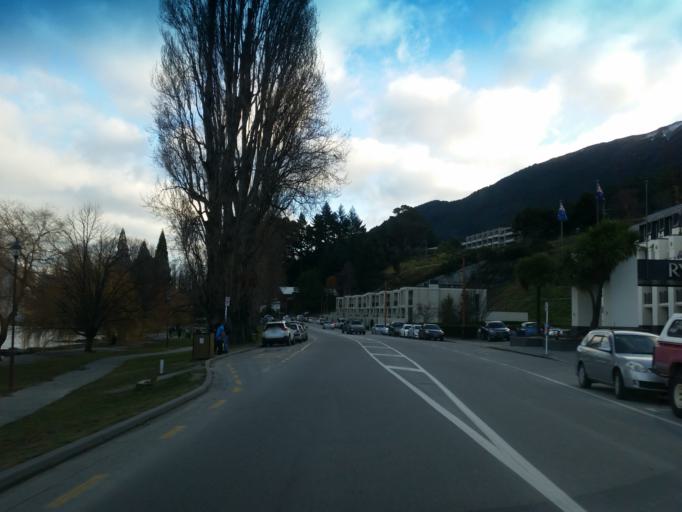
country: NZ
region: Otago
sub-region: Queenstown-Lakes District
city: Queenstown
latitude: -45.0352
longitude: 168.6525
